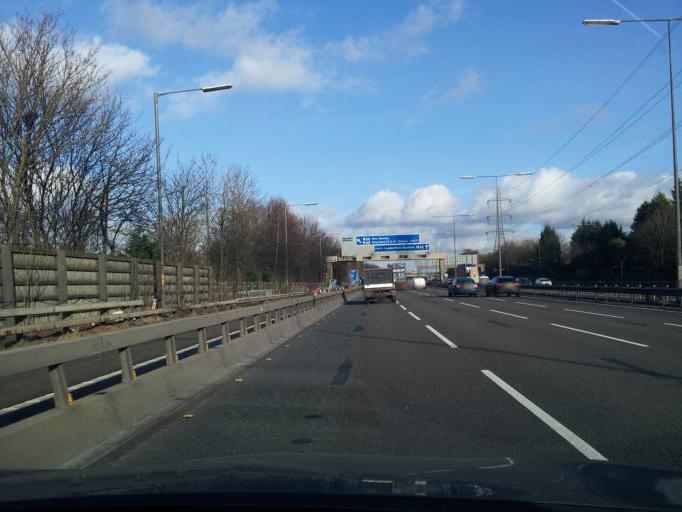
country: GB
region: England
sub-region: Borough of Bury
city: Prestwich
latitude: 53.5430
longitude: -2.2812
